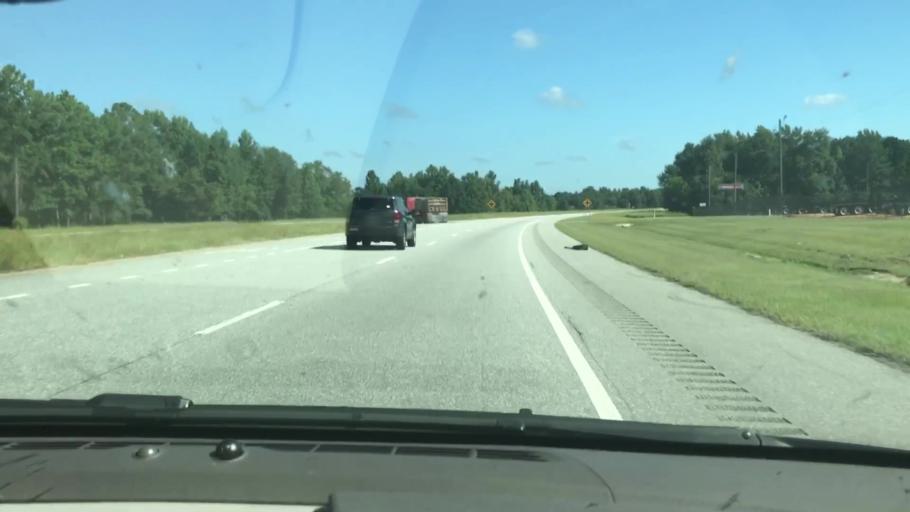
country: US
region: Alabama
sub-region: Russell County
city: Ladonia
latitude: 32.1905
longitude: -85.1815
